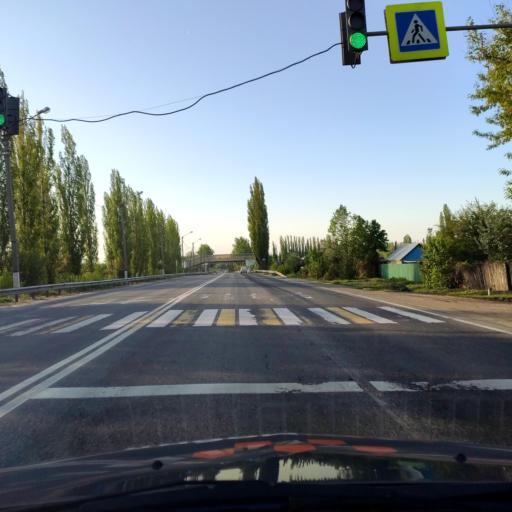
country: RU
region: Lipetsk
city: Yelets
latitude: 52.6021
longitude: 38.4709
